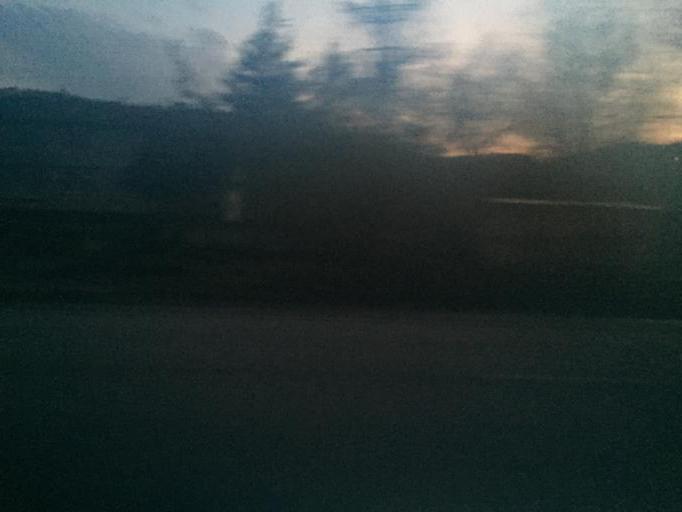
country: TR
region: Samsun
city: Kavak
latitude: 41.1339
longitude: 36.1288
